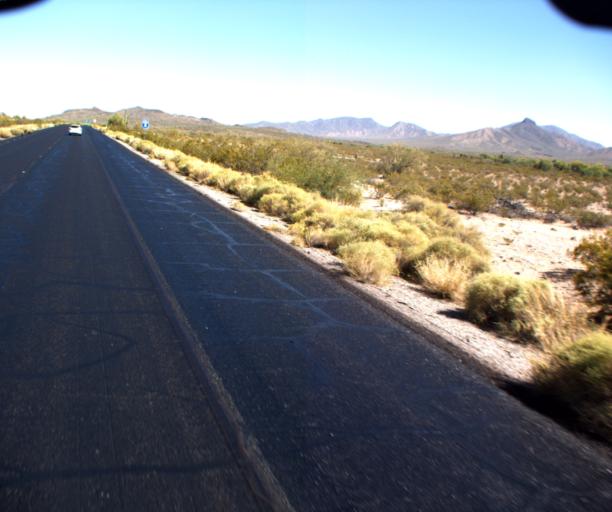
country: US
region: Arizona
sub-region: Pinal County
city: Maricopa
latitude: 32.8373
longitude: -112.2159
